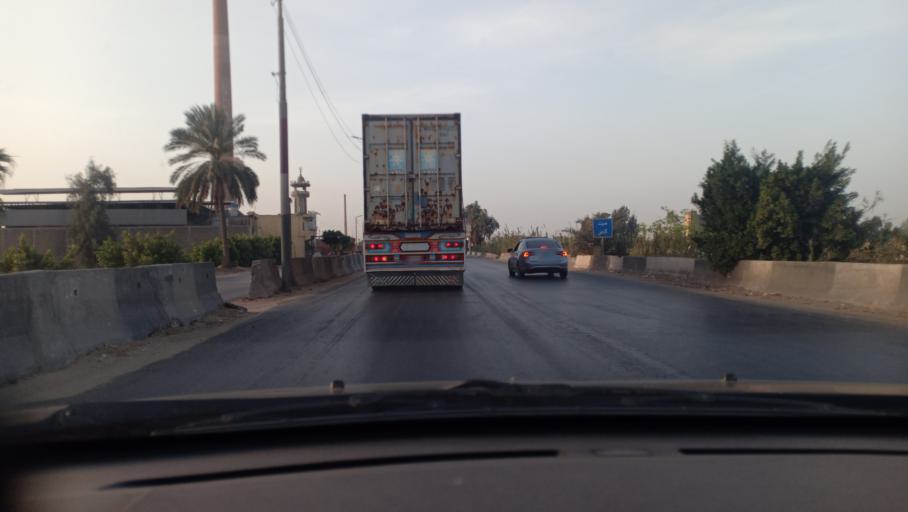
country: EG
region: Muhafazat al Gharbiyah
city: Zifta
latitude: 30.6054
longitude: 31.2750
